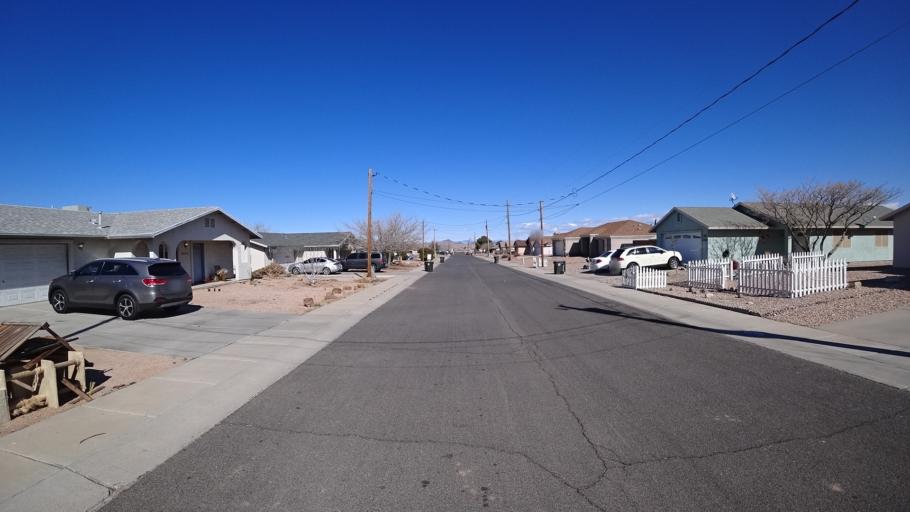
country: US
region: Arizona
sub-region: Mohave County
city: New Kingman-Butler
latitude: 35.2180
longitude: -114.0002
